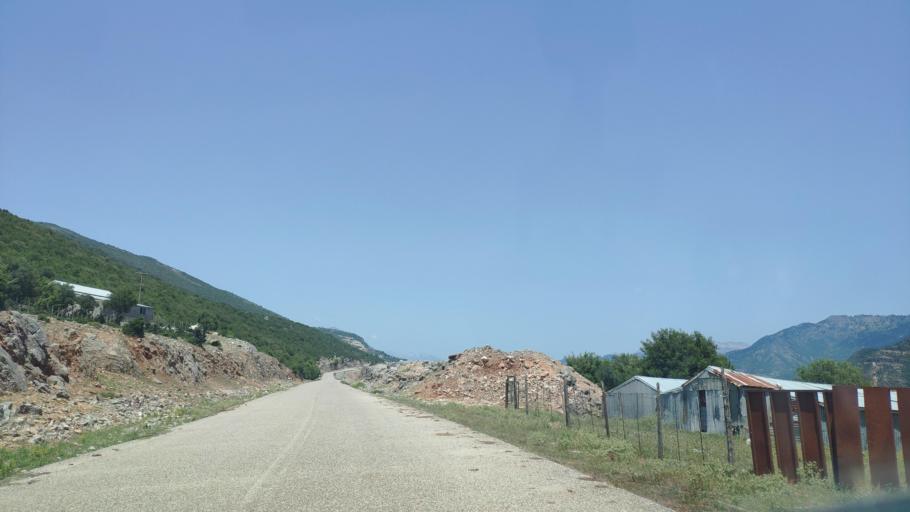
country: GR
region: Thessaly
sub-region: Nomos Kardhitsas
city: Anthiro
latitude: 39.1153
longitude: 21.4072
